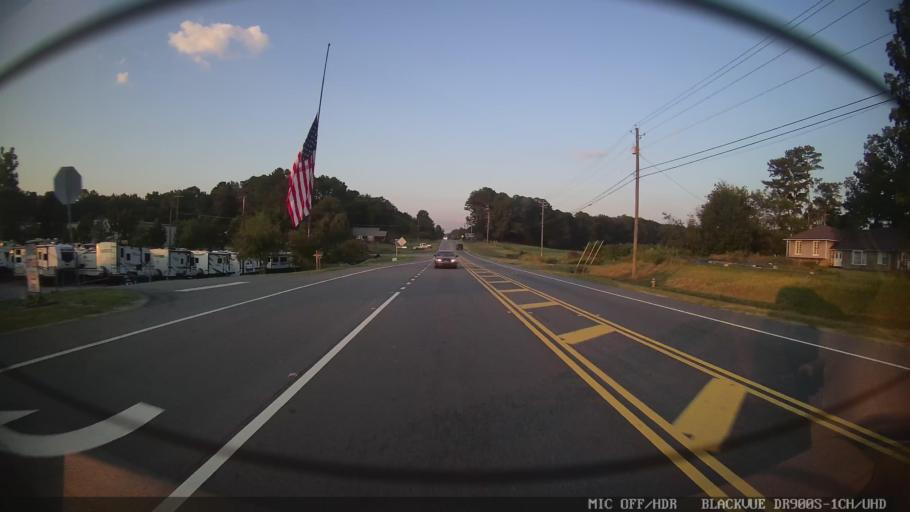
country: US
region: Georgia
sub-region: Bartow County
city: Rydal
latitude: 34.2675
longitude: -84.7551
